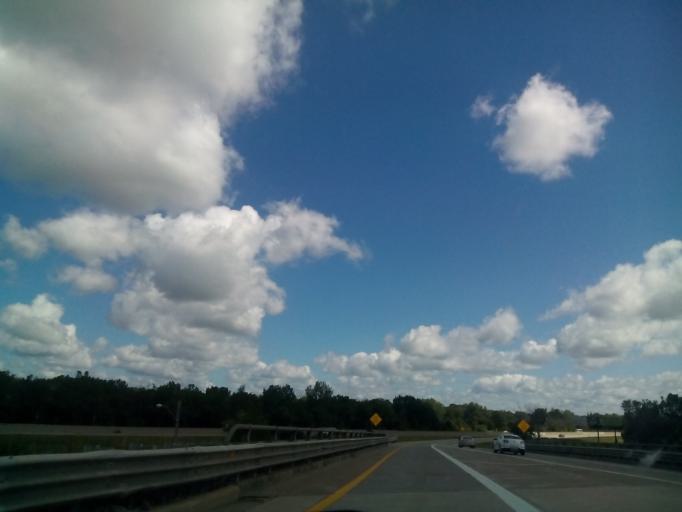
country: US
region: Michigan
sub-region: Genesee County
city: Flint
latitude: 42.9841
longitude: -83.7292
